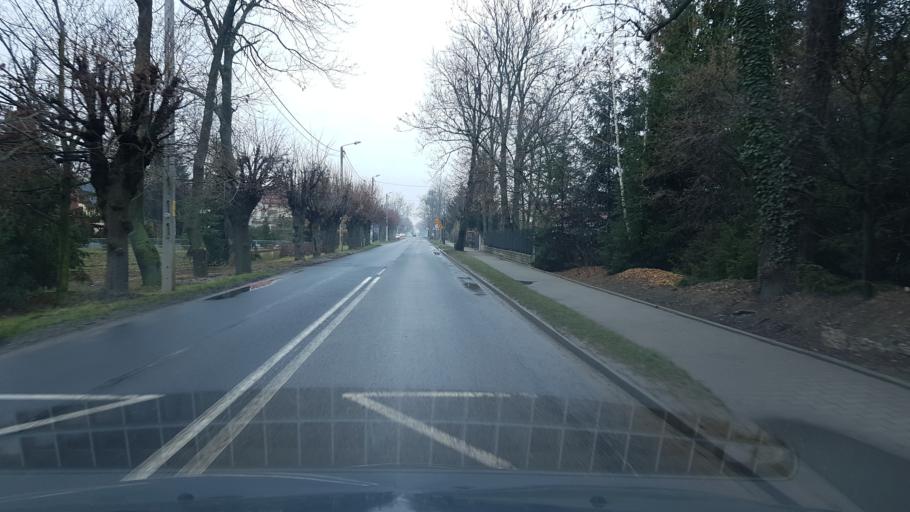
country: PL
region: Lower Silesian Voivodeship
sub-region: Powiat wroclawski
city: Bielany Wroclawskie
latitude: 50.9974
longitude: 16.9819
